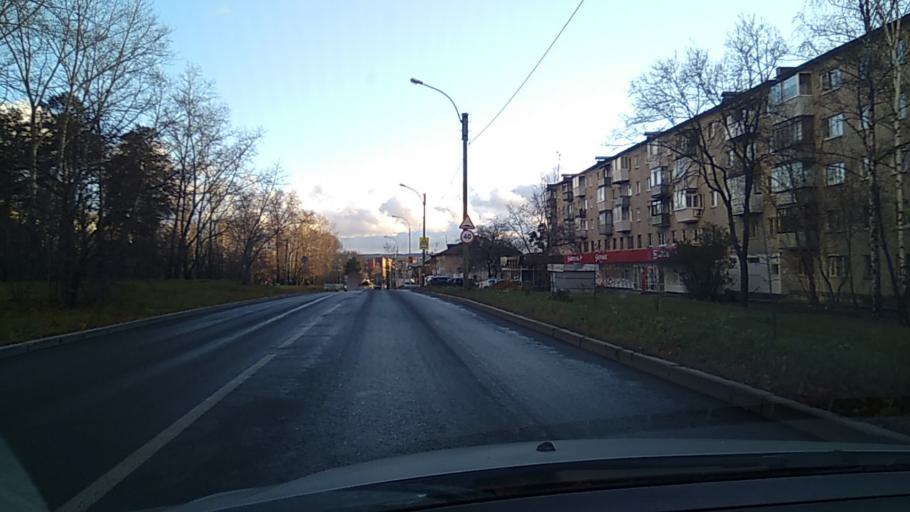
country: RU
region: Sverdlovsk
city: Sovkhoznyy
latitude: 56.7639
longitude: 60.6044
